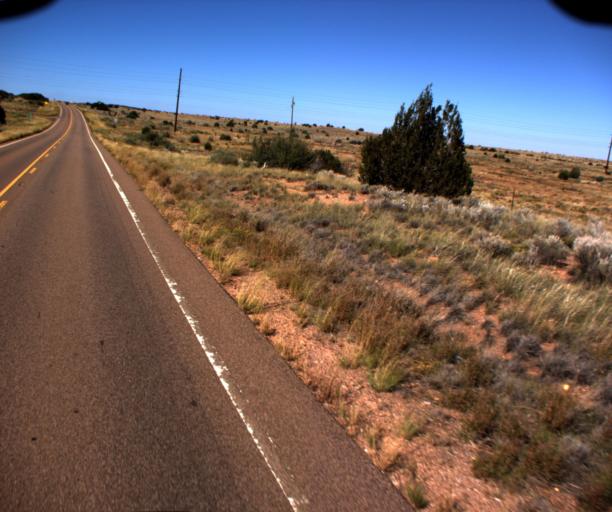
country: US
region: Arizona
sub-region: Navajo County
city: Taylor
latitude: 34.4831
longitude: -110.3235
